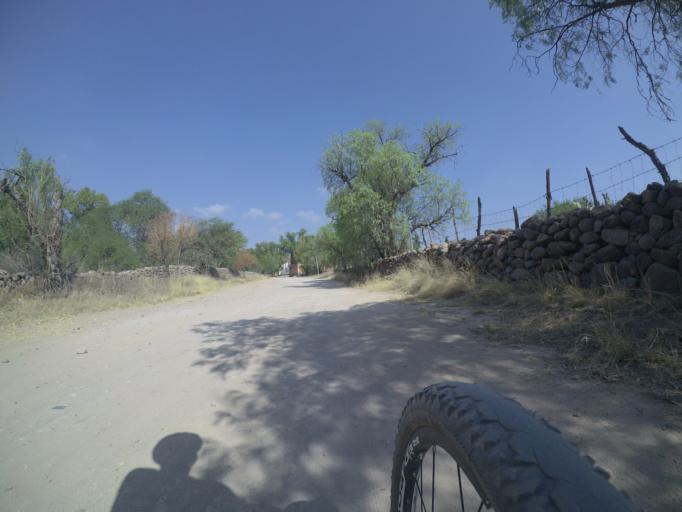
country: MX
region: Aguascalientes
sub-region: Jesus Maria
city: Paseos de las Haciendas [Fraccionamiento]
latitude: 21.9982
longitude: -102.3561
